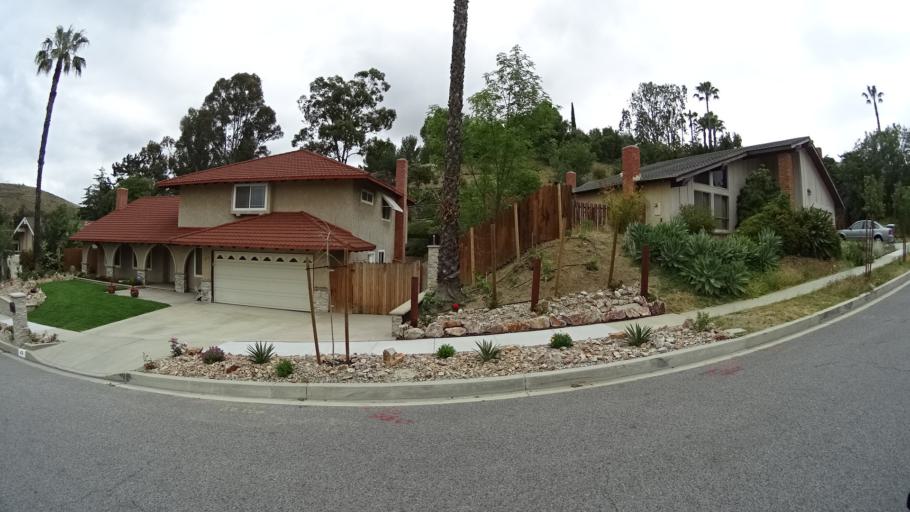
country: US
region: California
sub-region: Ventura County
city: Thousand Oaks
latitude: 34.2037
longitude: -118.8866
